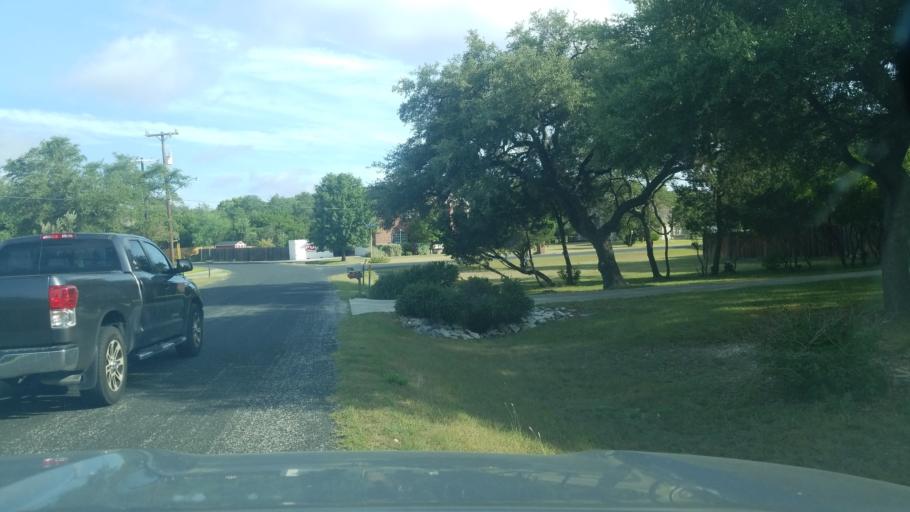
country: US
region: Texas
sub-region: Bexar County
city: Timberwood Park
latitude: 29.6811
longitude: -98.5062
